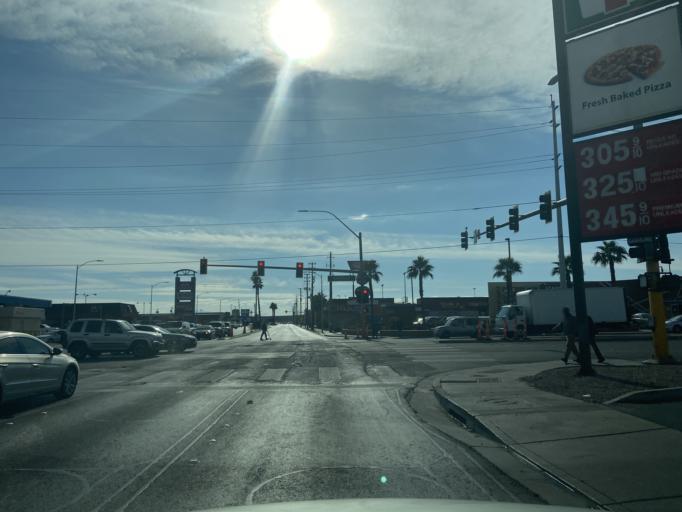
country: US
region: Nevada
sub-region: Clark County
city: Las Vegas
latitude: 36.1743
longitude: -115.1163
